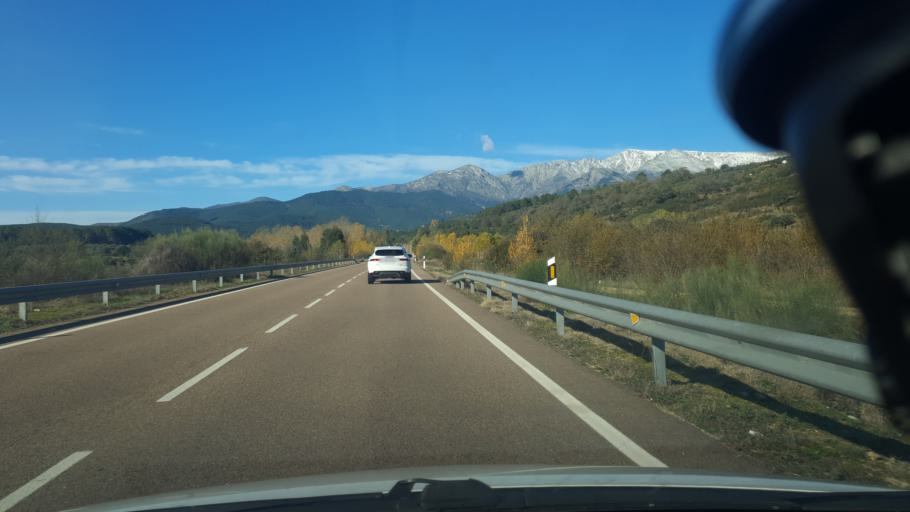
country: ES
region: Castille and Leon
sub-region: Provincia de Avila
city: Arenas de San Pedro
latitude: 40.1867
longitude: -5.0590
